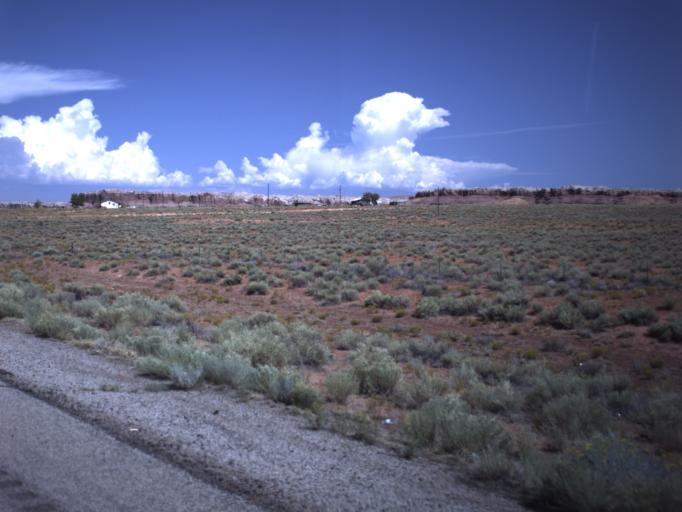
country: US
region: Utah
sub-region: San Juan County
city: Blanding
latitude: 37.1693
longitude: -109.5792
